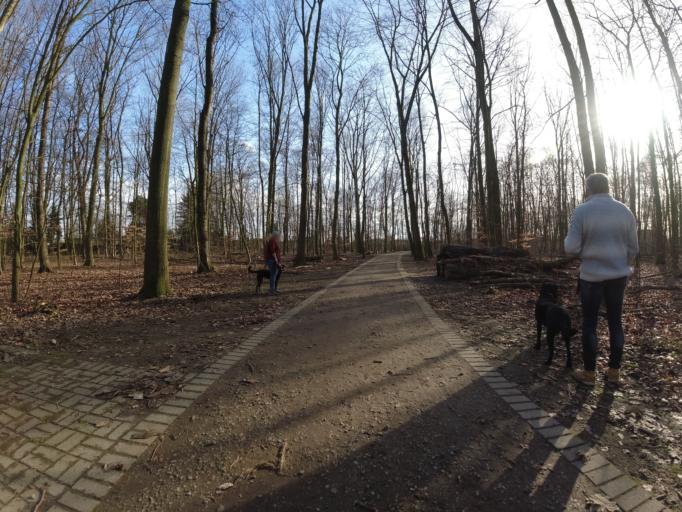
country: DE
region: North Rhine-Westphalia
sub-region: Regierungsbezirk Dusseldorf
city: Hochfeld
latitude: 51.4041
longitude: 6.6951
